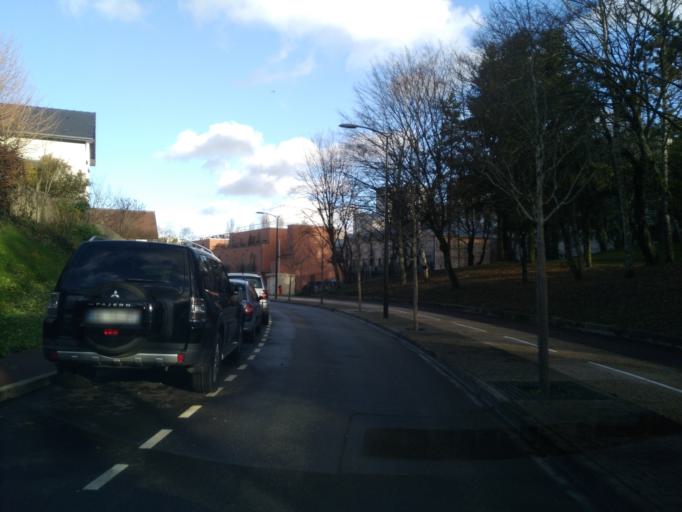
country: FR
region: Ile-de-France
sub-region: Departement des Yvelines
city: Fourqueux
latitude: 48.8952
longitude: 2.0659
